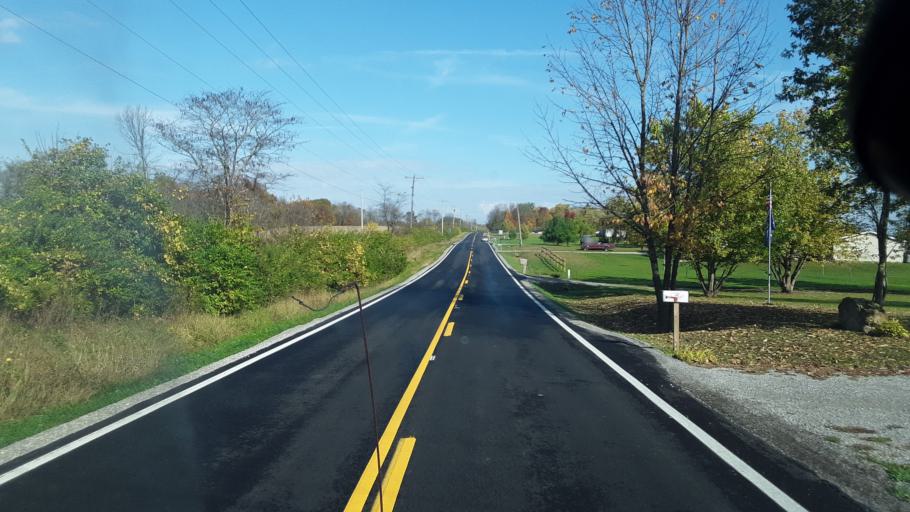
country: US
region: Ohio
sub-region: Highland County
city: Leesburg
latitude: 39.3700
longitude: -83.5932
